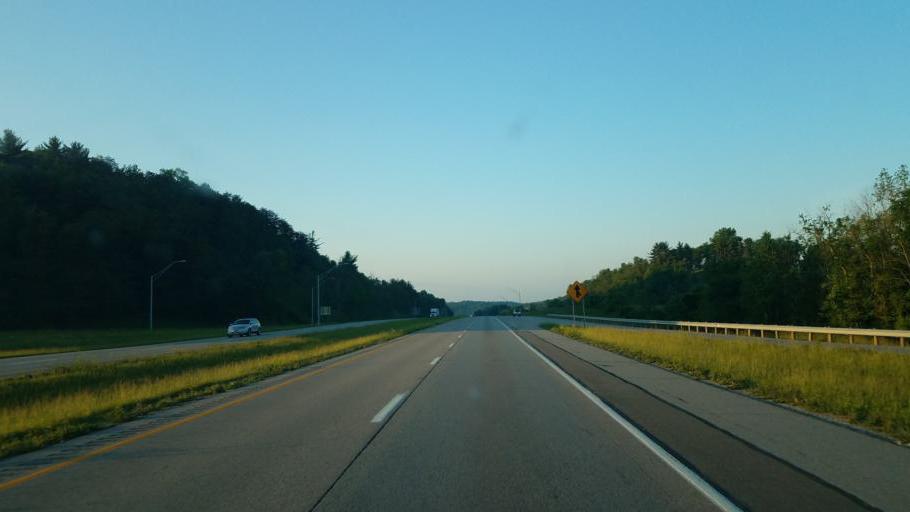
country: US
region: Ohio
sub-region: Washington County
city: Devola
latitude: 39.4848
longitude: -81.4429
